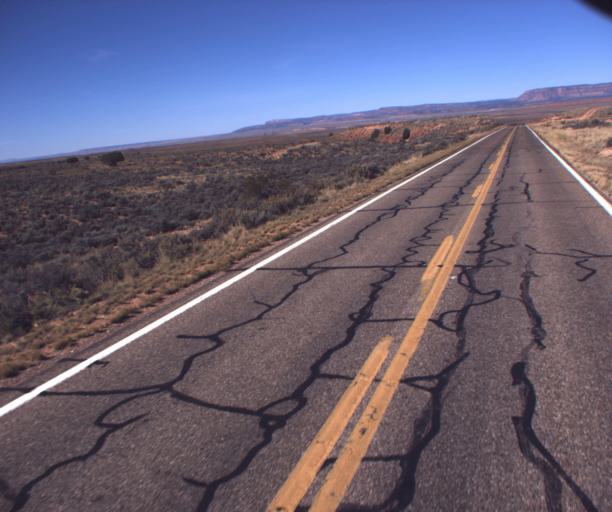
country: US
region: Arizona
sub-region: Coconino County
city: Fredonia
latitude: 36.9058
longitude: -112.3913
